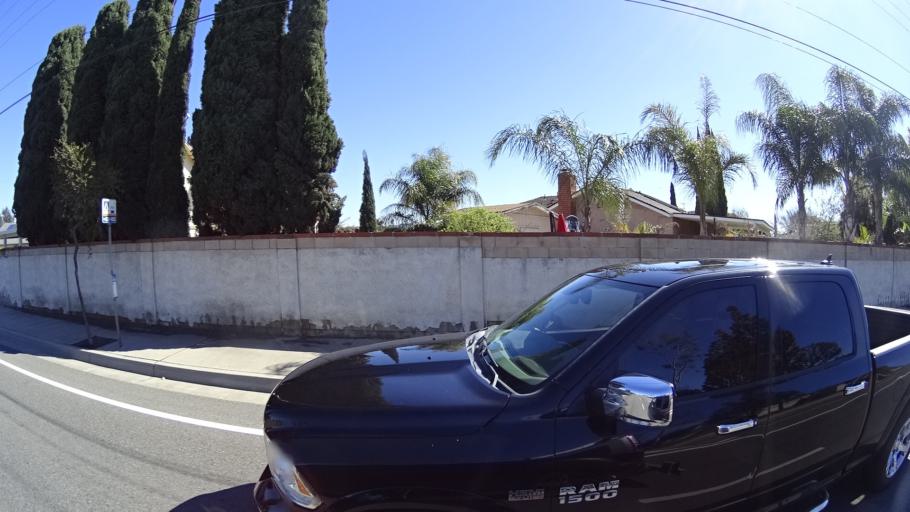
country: US
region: California
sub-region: Orange County
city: Placentia
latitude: 33.8329
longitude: -117.8618
